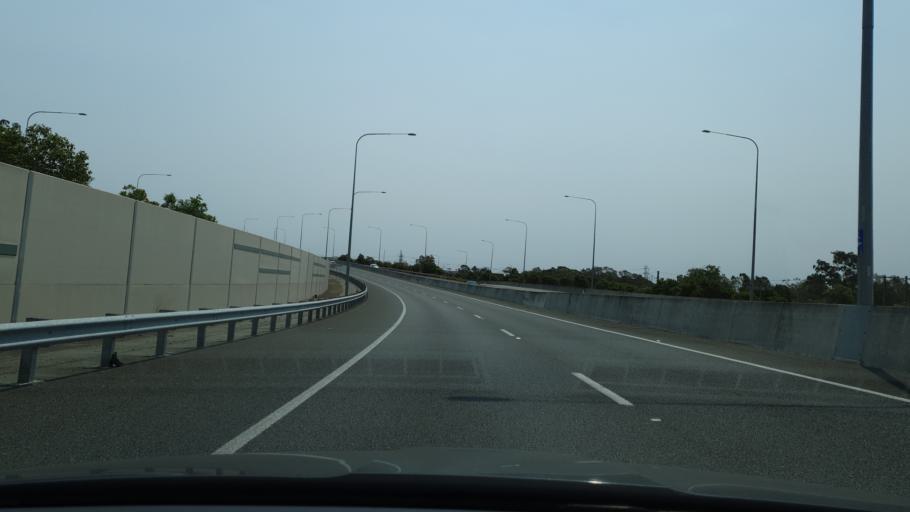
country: AU
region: Queensland
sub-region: Ipswich
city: Riverview
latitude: -27.5958
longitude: 152.8389
